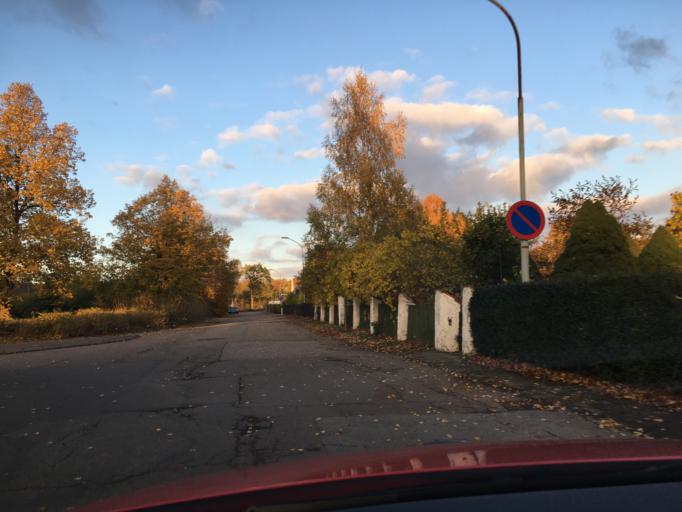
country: SE
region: Skane
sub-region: Bjuvs Kommun
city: Bjuv
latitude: 56.0814
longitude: 12.9257
